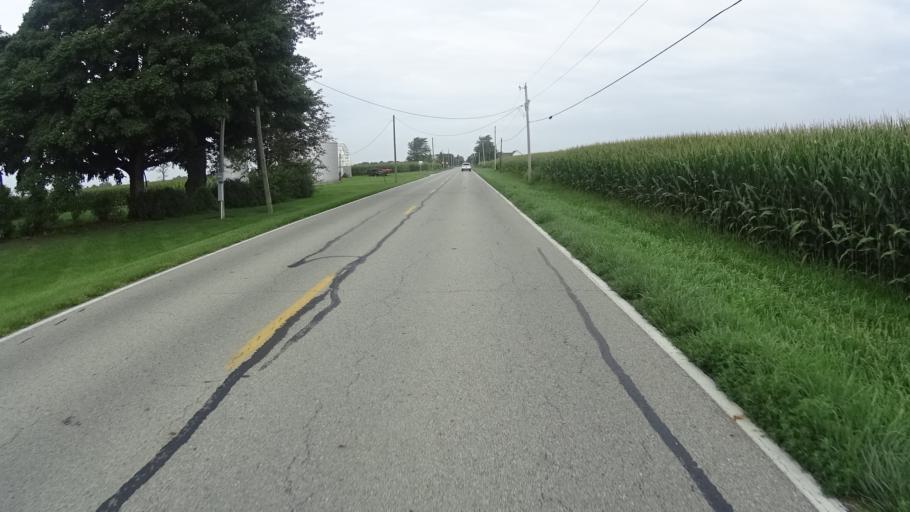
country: US
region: Indiana
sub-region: Madison County
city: Lapel
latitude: 40.0534
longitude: -85.8265
